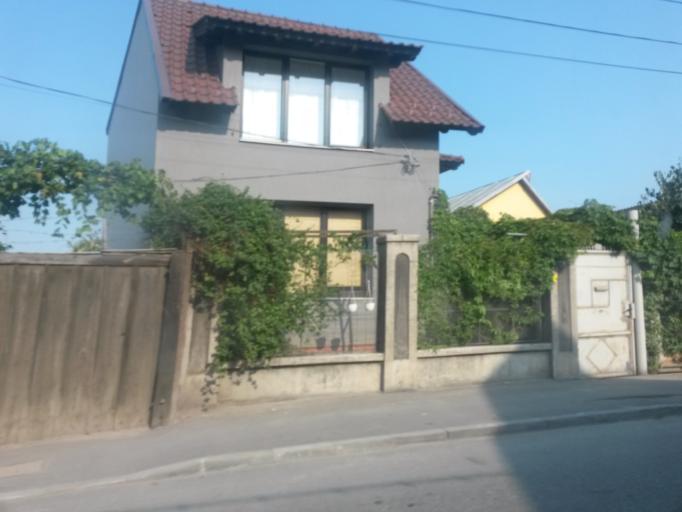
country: RO
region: Cluj
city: Turda
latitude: 46.5712
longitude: 23.7800
